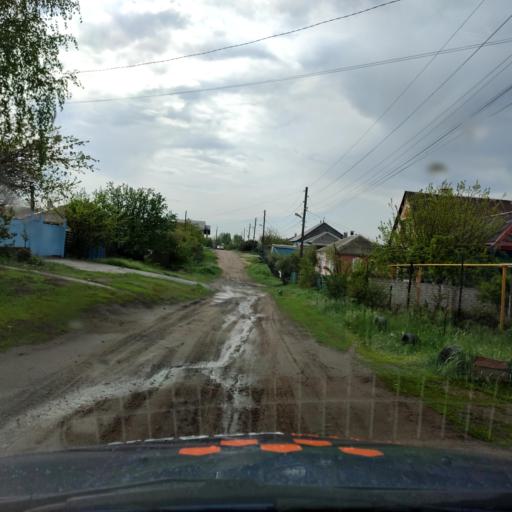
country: RU
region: Voronezj
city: Maslovka
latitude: 51.5520
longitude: 39.2340
